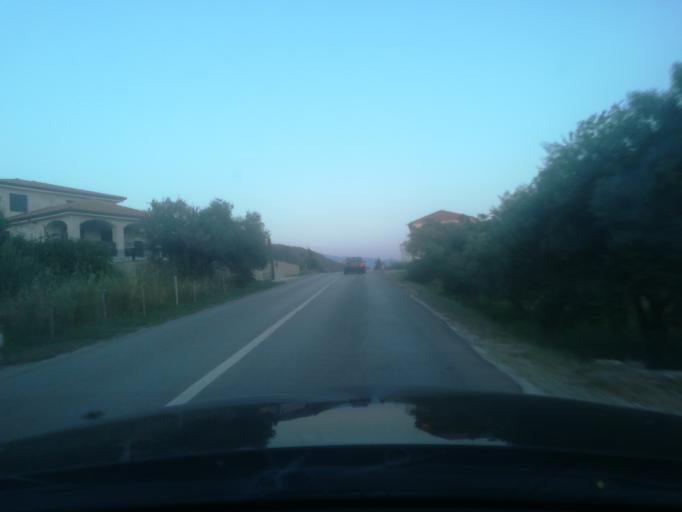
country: HR
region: Primorsko-Goranska
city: Banjol
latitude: 44.7520
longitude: 14.7822
